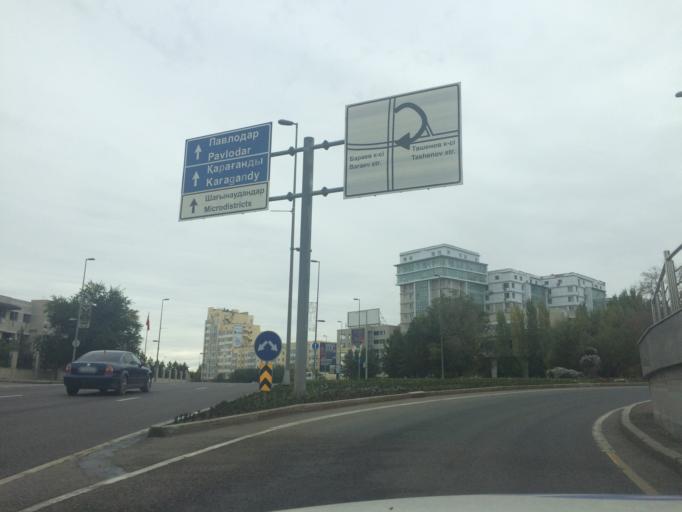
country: KZ
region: Astana Qalasy
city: Astana
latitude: 51.1533
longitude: 71.4326
